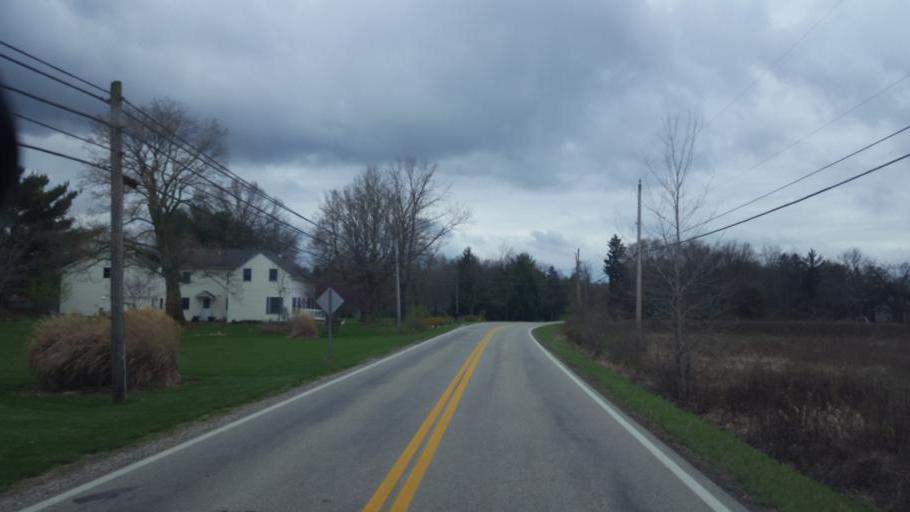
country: US
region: Ohio
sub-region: Delaware County
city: Sunbury
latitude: 40.2255
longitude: -82.8717
